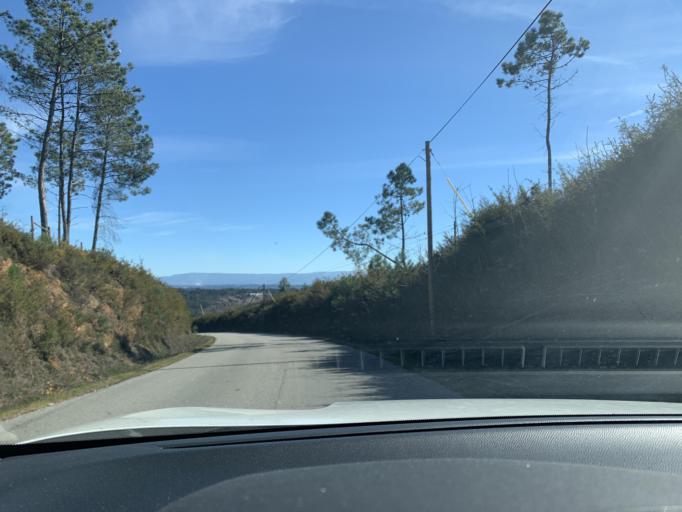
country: PT
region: Viseu
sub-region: Concelho de Tondela
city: Tondela
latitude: 40.6052
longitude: -8.0418
